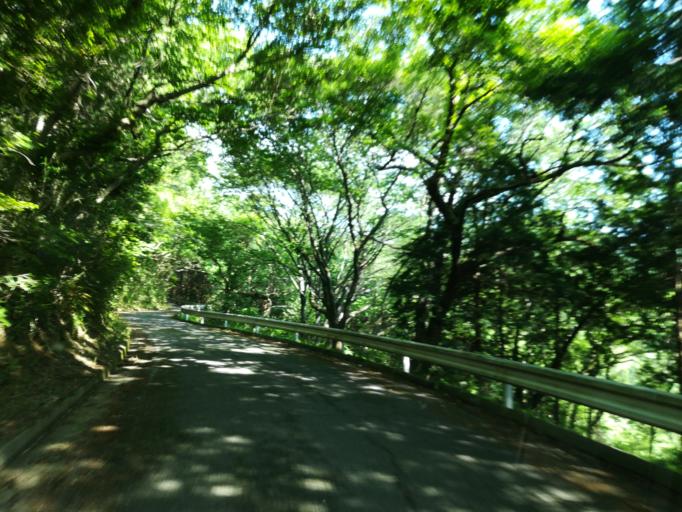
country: JP
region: Ibaraki
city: Tsukuba
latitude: 36.1819
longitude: 140.1325
